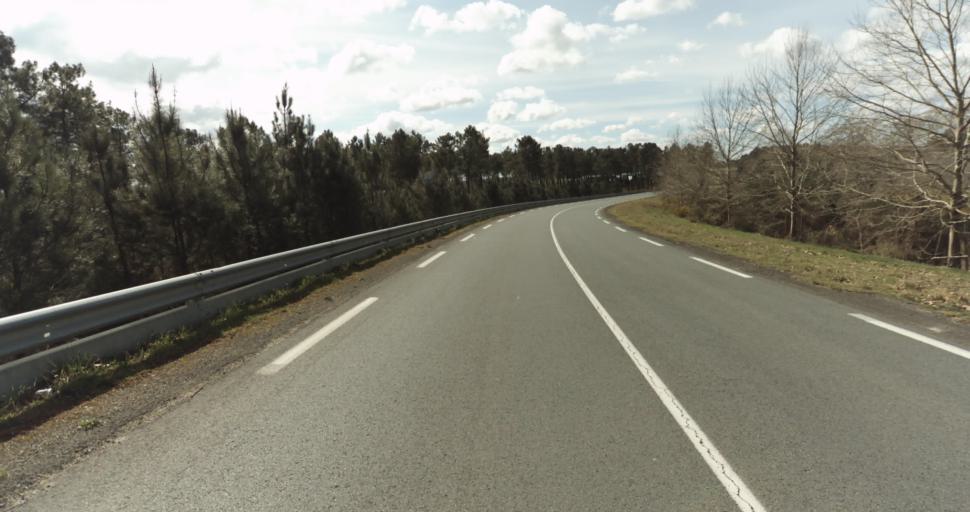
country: FR
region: Aquitaine
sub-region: Departement des Landes
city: Roquefort
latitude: 44.0575
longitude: -0.3165
